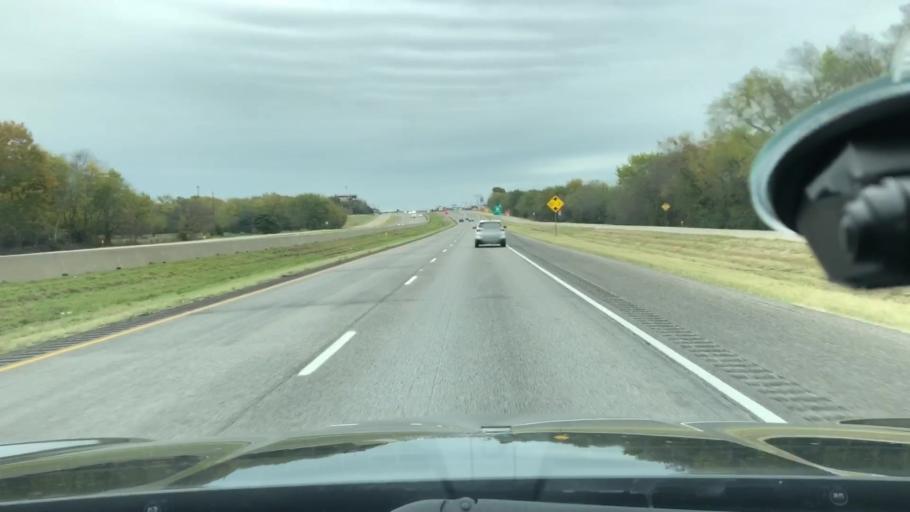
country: US
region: Texas
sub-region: Hunt County
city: Commerce
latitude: 33.1291
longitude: -95.8486
